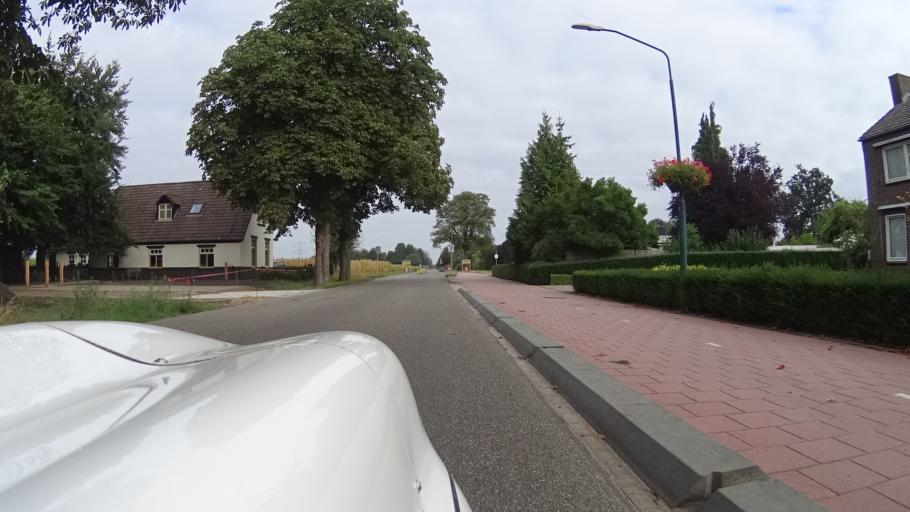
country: NL
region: North Brabant
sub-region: Gemeente Sint Anthonis
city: Sint Anthonis
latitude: 51.6042
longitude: 5.9145
